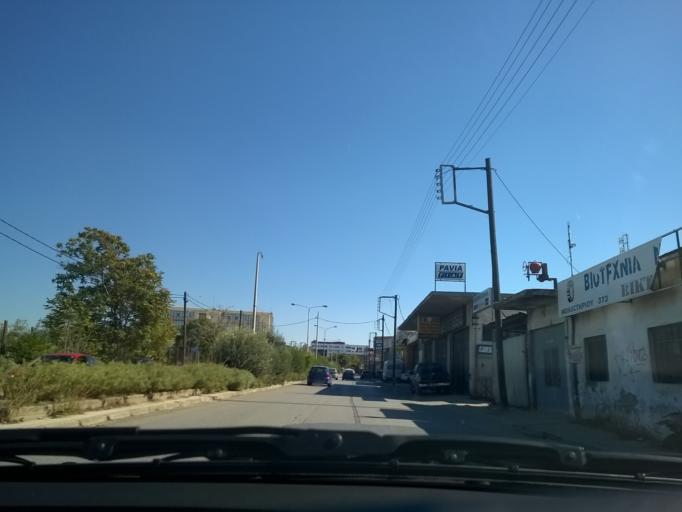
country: GR
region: Central Macedonia
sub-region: Nomos Thessalonikis
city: Menemeni
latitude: 40.6597
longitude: 22.9003
